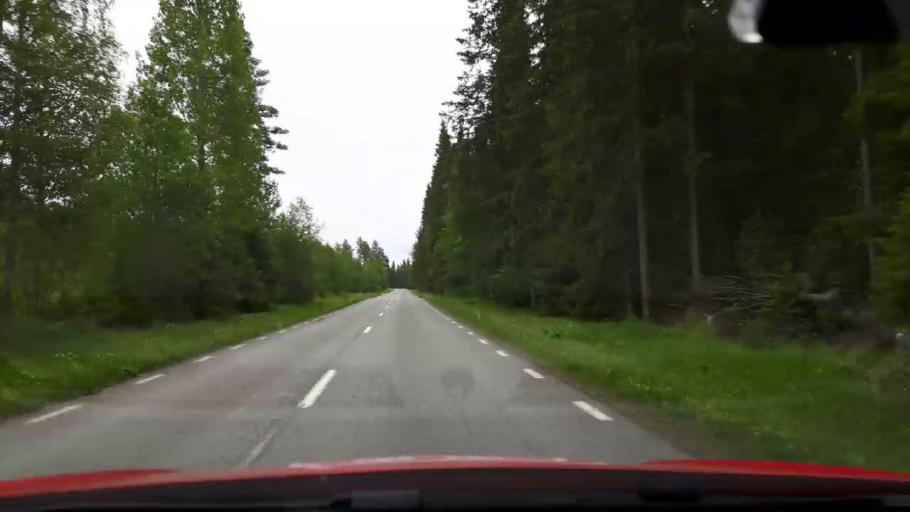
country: SE
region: Jaemtland
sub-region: Stroemsunds Kommun
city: Stroemsund
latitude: 63.4264
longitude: 15.5104
